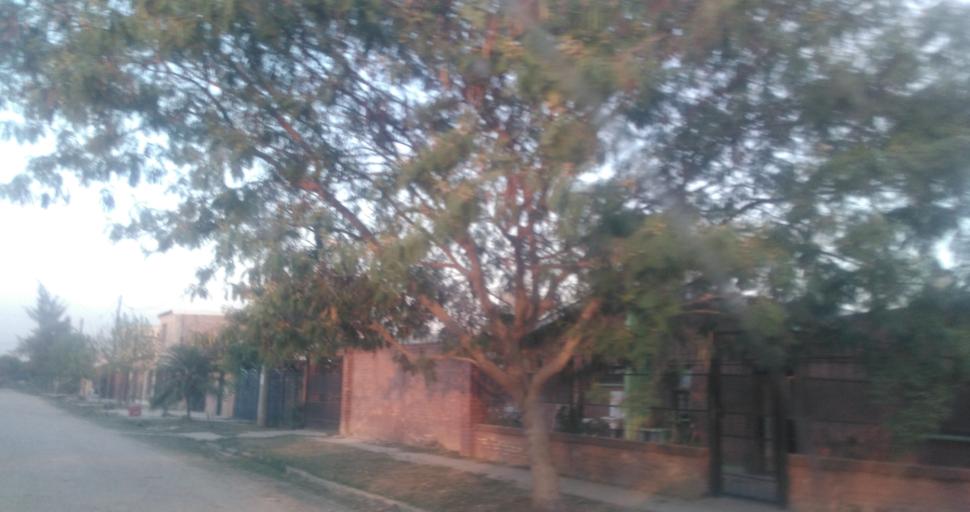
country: AR
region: Chaco
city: Resistencia
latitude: -27.4779
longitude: -59.0067
